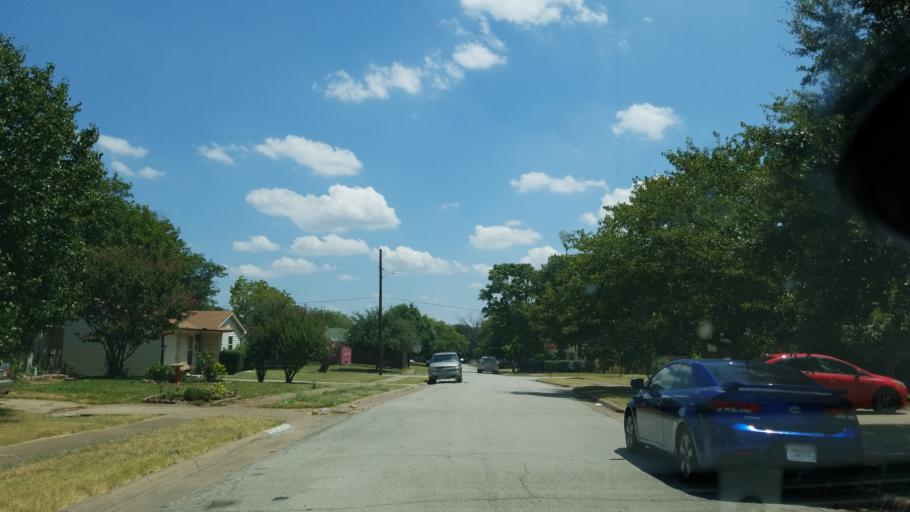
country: US
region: Texas
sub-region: Dallas County
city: Duncanville
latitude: 32.6650
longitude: -96.8958
